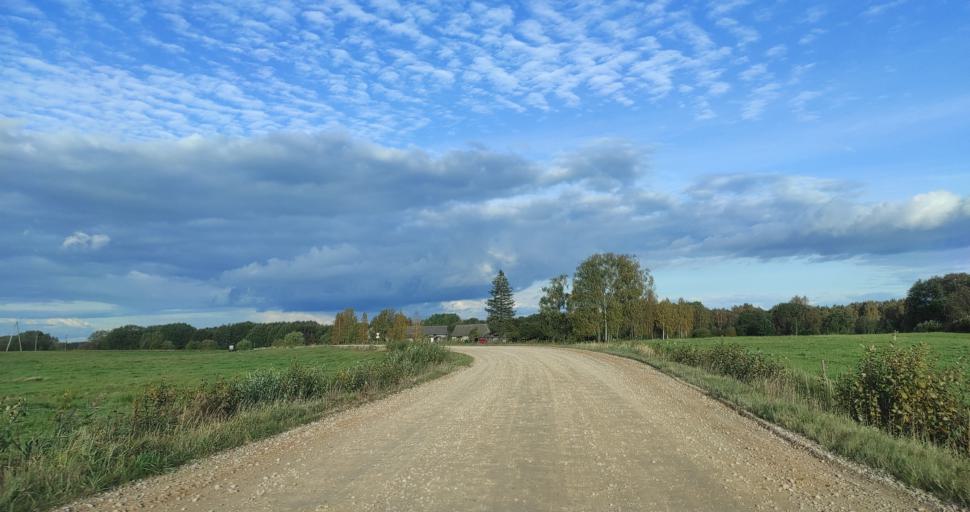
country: LV
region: Aizpute
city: Aizpute
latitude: 56.7493
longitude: 21.7909
